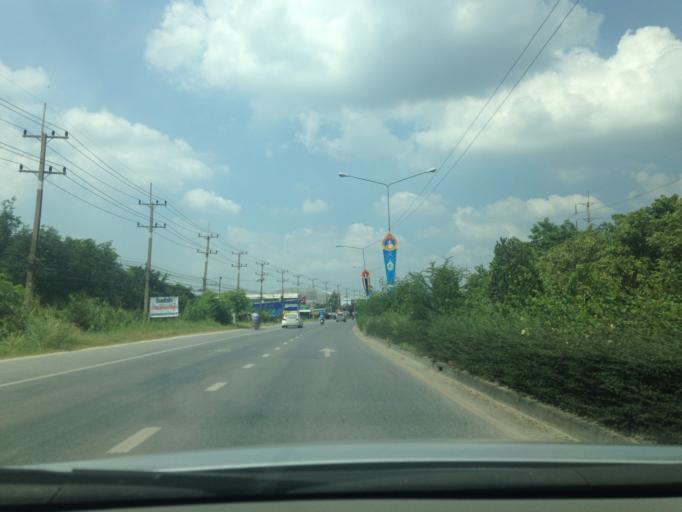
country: TH
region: Pathum Thani
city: Sam Khok
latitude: 14.0716
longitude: 100.5216
